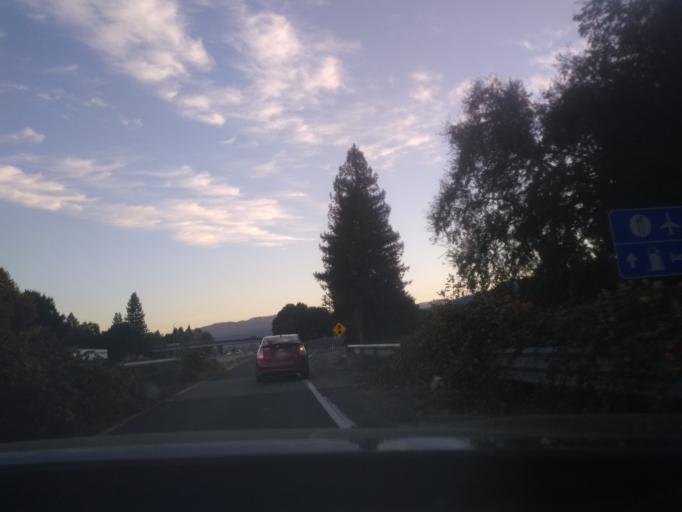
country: US
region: California
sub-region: Mendocino County
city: Ukiah
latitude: 39.1381
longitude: -123.1962
